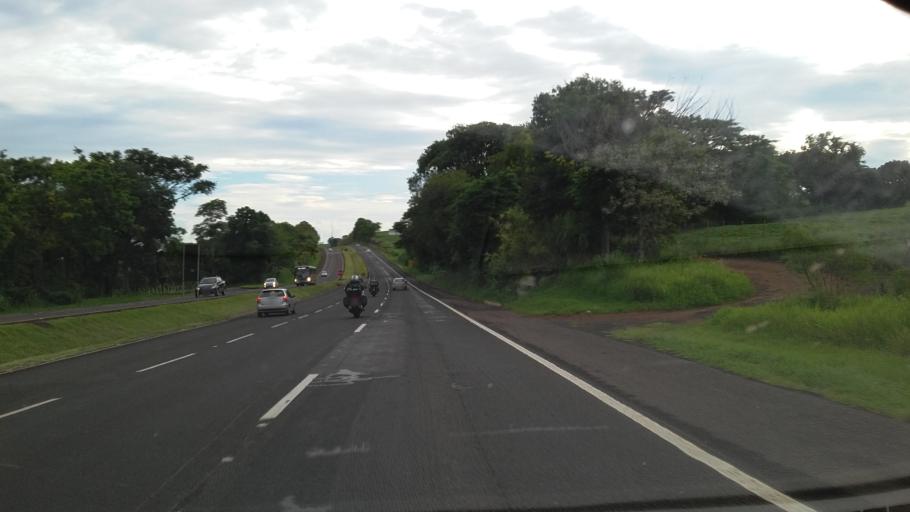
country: BR
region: Parana
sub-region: Paicandu
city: Paicandu
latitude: -23.5112
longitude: -52.0245
